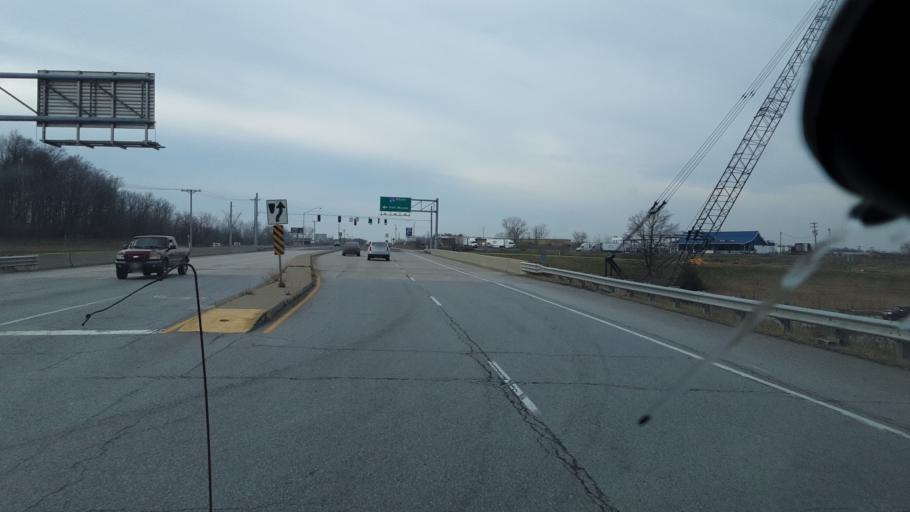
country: US
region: Indiana
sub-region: DeKalb County
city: Waterloo
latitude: 41.4397
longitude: -85.0526
